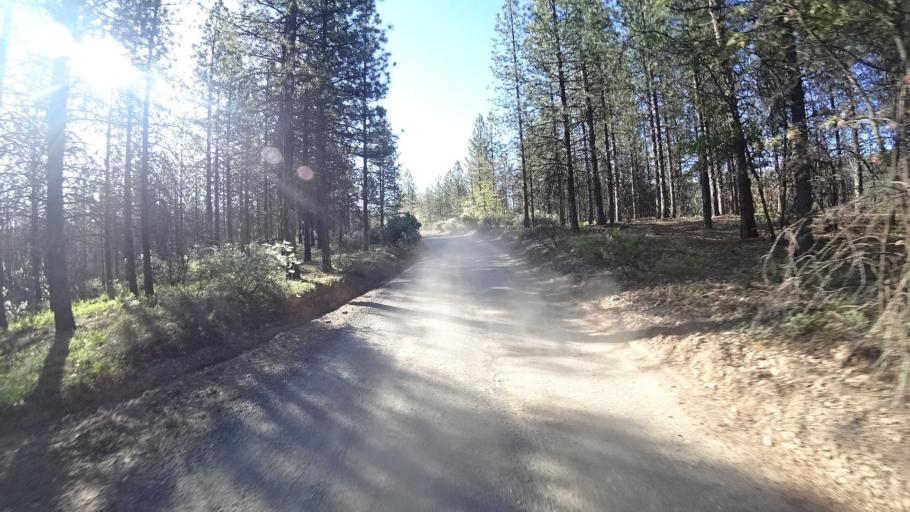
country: US
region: California
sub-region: Lake County
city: Upper Lake
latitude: 39.3245
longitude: -122.9502
